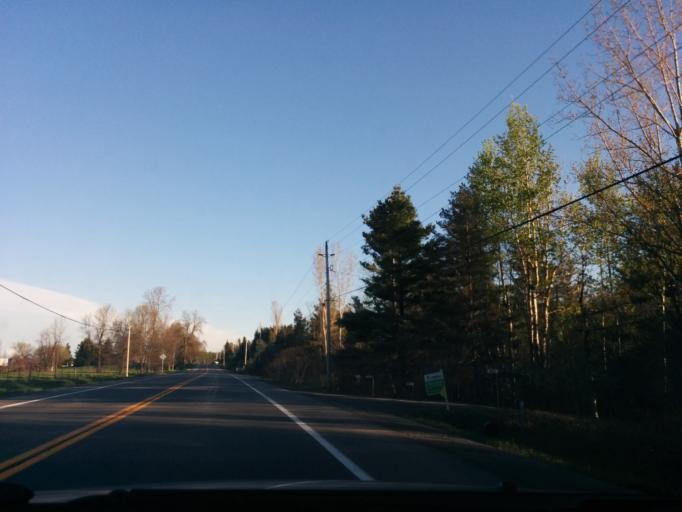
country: CA
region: Ontario
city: Ottawa
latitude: 45.1782
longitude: -75.6257
